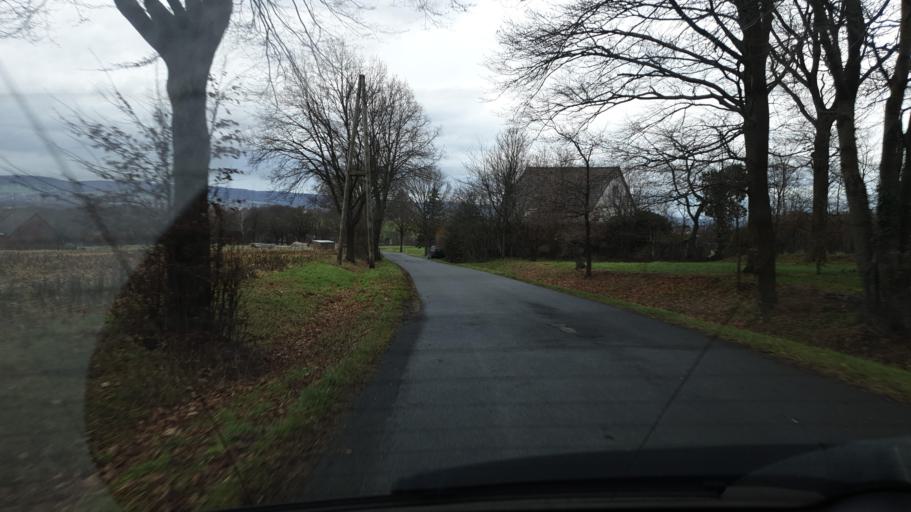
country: DE
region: North Rhine-Westphalia
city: Bad Oeynhausen
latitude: 52.1710
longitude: 8.7838
